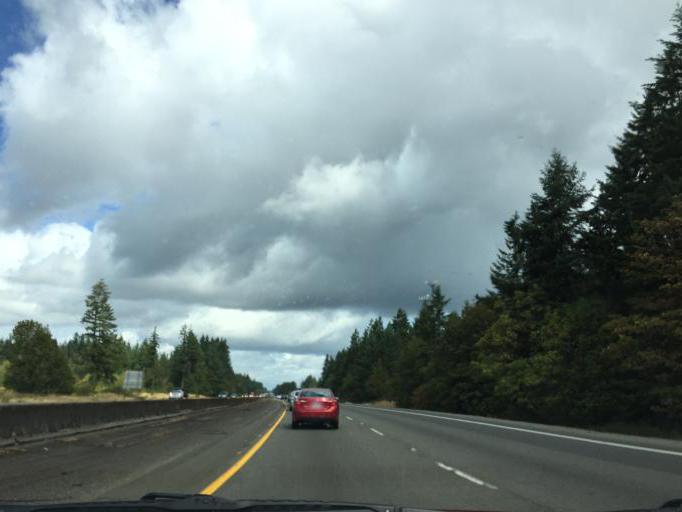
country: US
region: Washington
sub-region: Lewis County
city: Winlock
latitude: 46.4941
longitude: -122.8766
